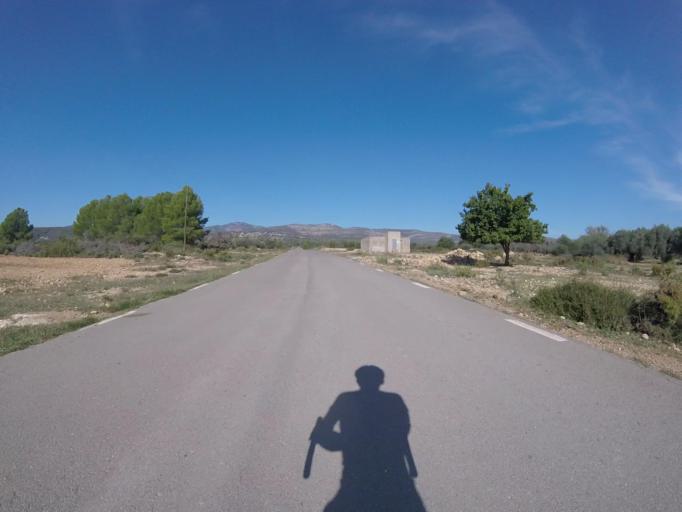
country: ES
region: Valencia
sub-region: Provincia de Castello
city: Sarratella
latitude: 40.2680
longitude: 0.0637
